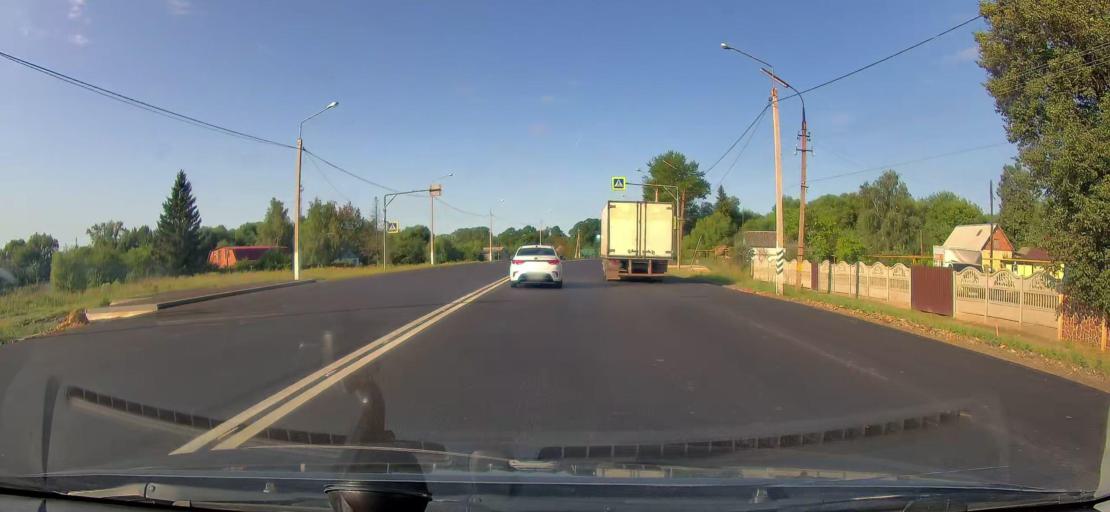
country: RU
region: Tula
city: Bol'shoye Skuratovo
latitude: 53.3977
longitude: 36.7602
